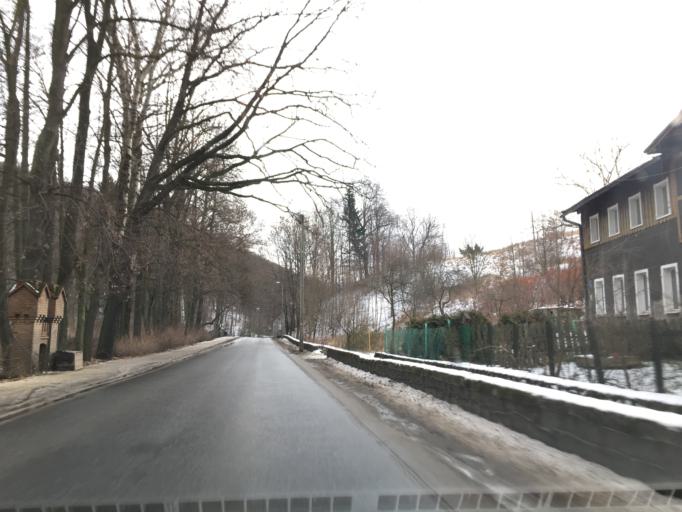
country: PL
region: Lower Silesian Voivodeship
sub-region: Powiat walbrzyski
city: Dziecmorowice
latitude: 50.7512
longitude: 16.4057
